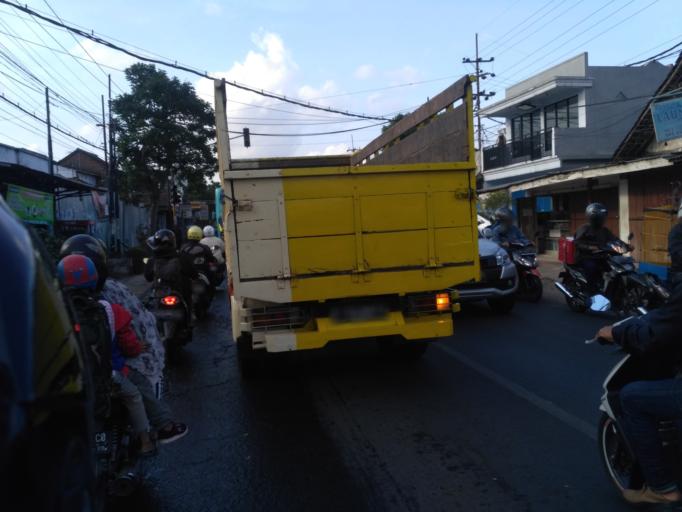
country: ID
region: East Java
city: Kebonsari
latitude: -8.0208
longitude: 112.6188
